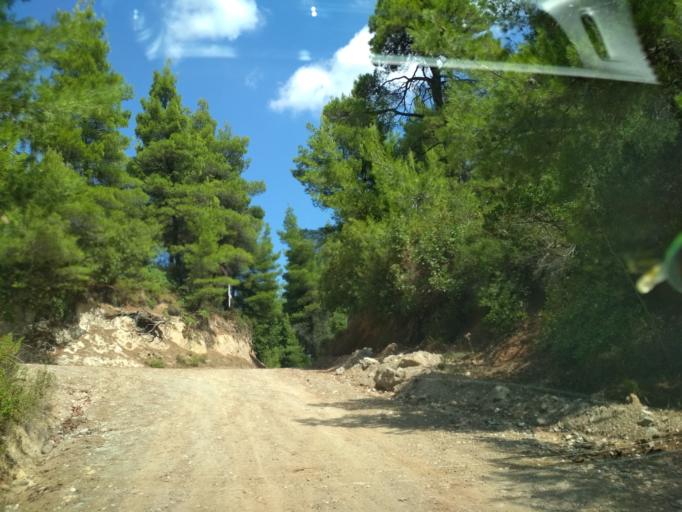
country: GR
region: Central Greece
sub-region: Nomos Evvoias
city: Roviai
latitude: 38.8409
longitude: 23.2796
